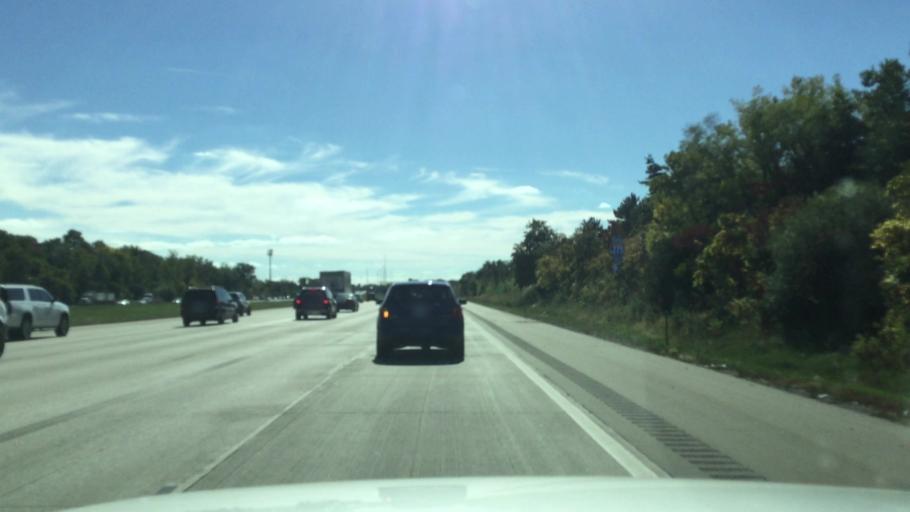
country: US
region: Michigan
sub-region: Wayne County
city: Plymouth
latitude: 42.4041
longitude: -83.4264
